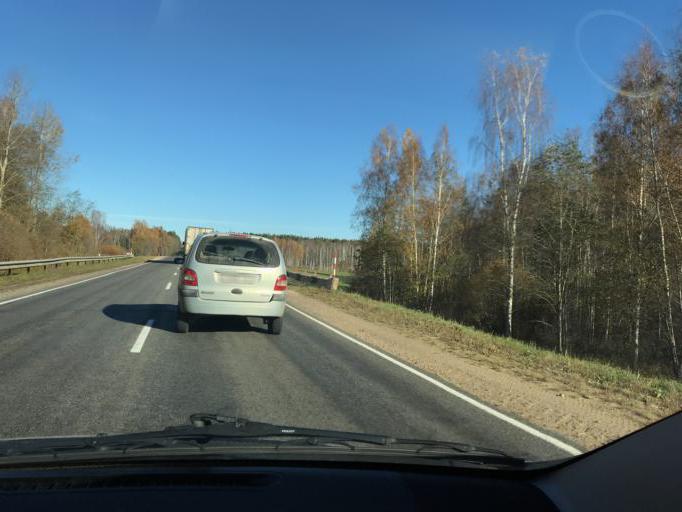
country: BY
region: Vitebsk
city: Polatsk
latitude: 55.3332
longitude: 28.7884
